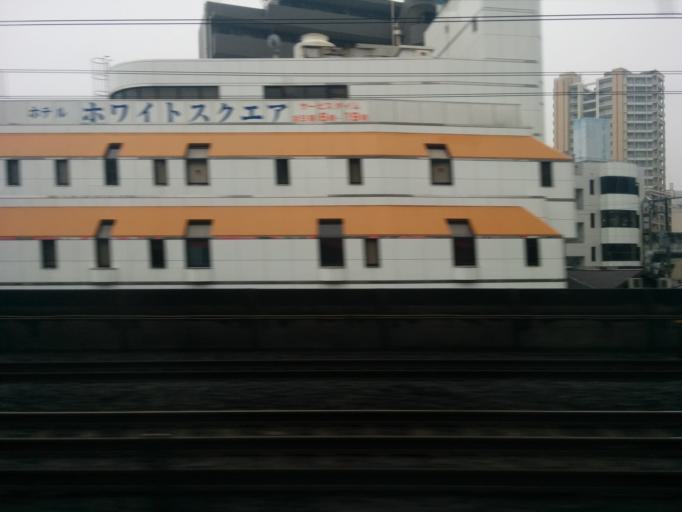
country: JP
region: Chiba
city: Funabashi
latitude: 35.7015
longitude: 139.9878
